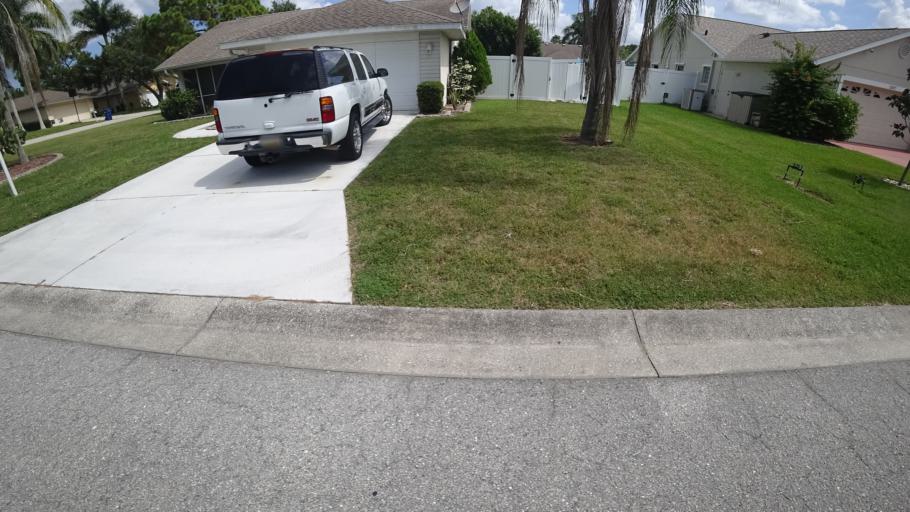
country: US
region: Florida
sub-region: Manatee County
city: Samoset
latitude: 27.4537
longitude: -82.5350
